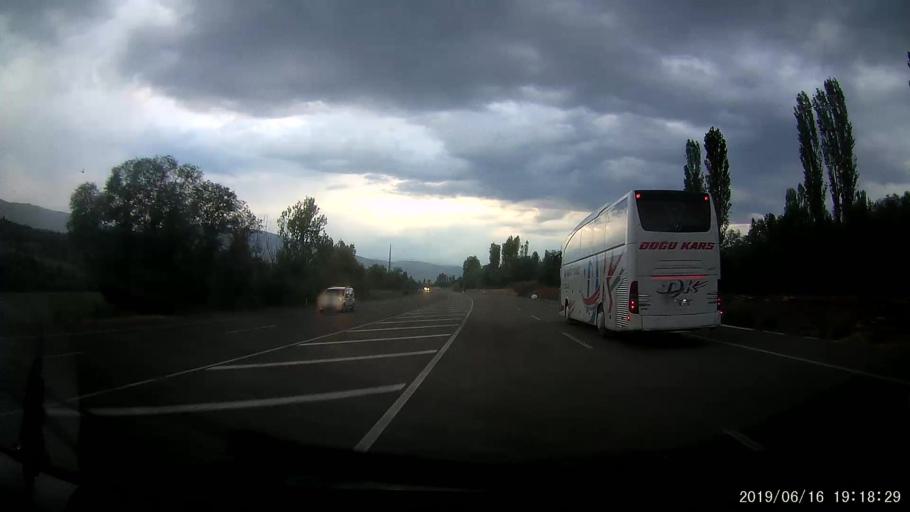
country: TR
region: Sivas
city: Akincilar
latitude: 40.0953
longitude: 38.4563
